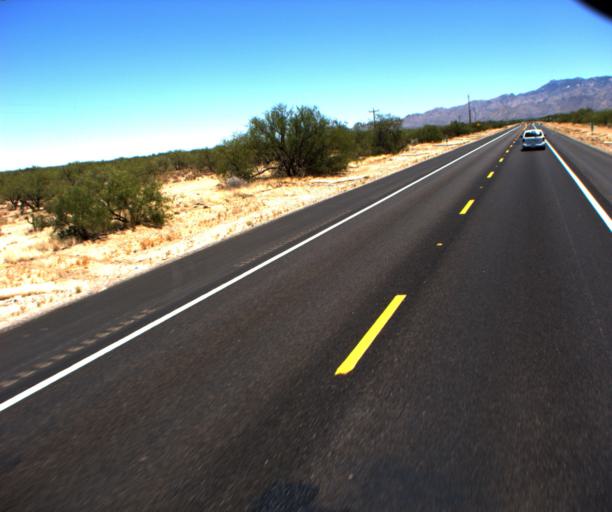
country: US
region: Arizona
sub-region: Pima County
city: Sells
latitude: 31.9265
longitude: -111.7988
